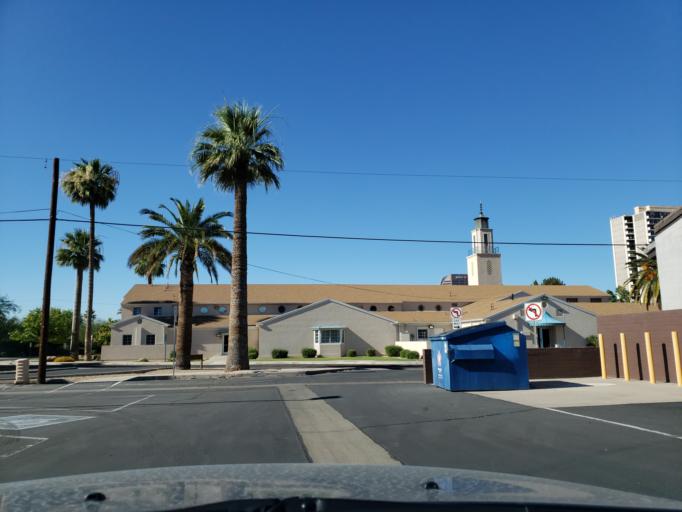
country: US
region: Arizona
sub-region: Maricopa County
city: Phoenix
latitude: 33.4759
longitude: -112.0709
